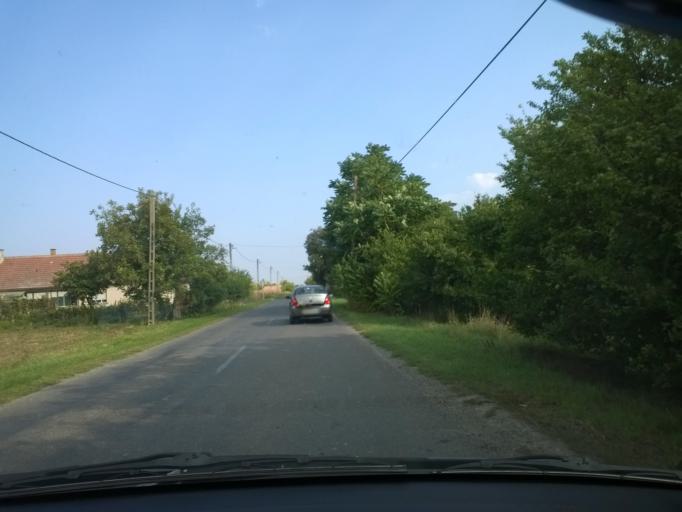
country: HU
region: Bacs-Kiskun
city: Kalocsa
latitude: 46.4994
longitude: 19.0528
